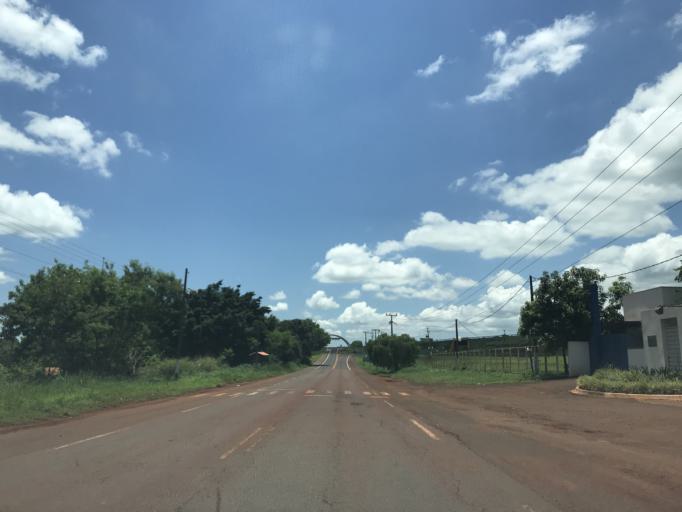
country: BR
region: Parana
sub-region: Marialva
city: Marialva
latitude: -23.4982
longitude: -51.7741
